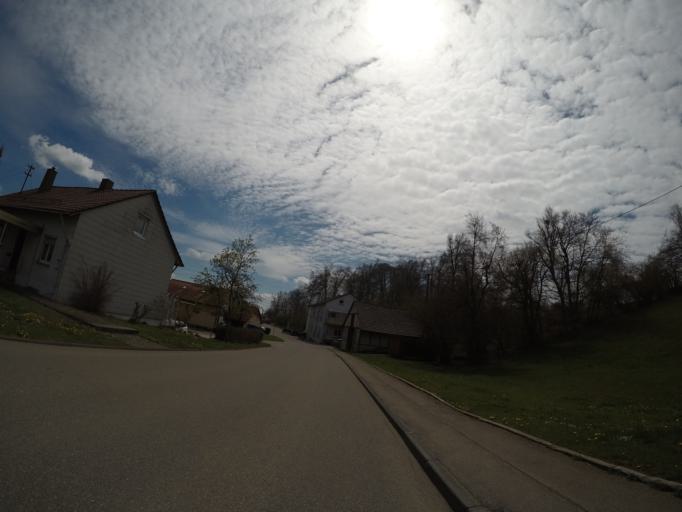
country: DE
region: Baden-Wuerttemberg
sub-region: Tuebingen Region
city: Westerheim
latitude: 48.5122
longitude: 9.6263
